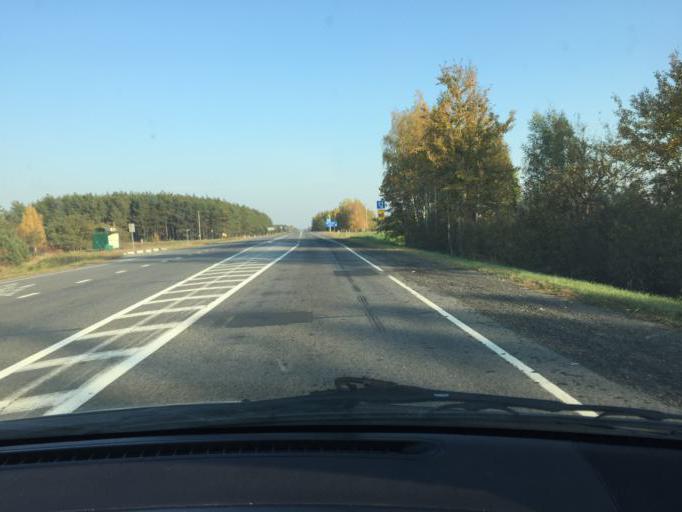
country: BY
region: Brest
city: Davyd-Haradok
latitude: 52.2450
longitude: 27.1366
